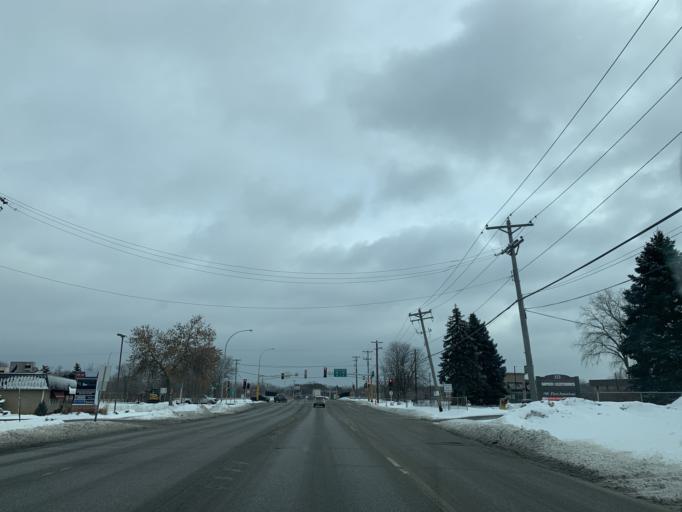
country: US
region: Minnesota
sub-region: Ramsey County
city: Little Canada
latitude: 45.0236
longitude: -93.0922
